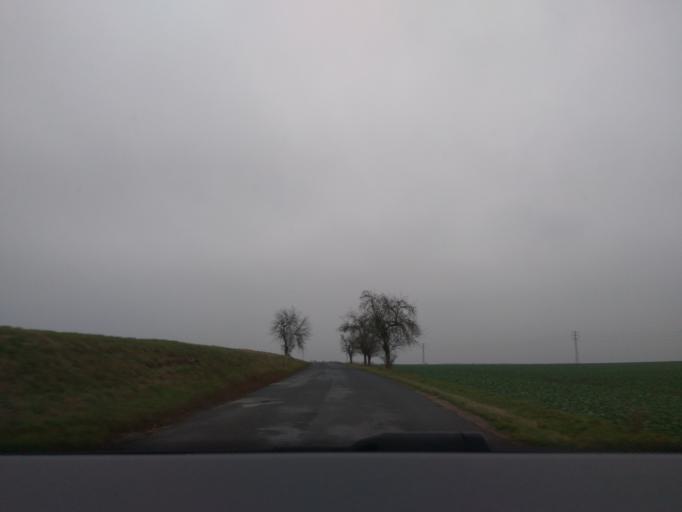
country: CZ
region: Praha
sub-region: Praha 19
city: Kbely
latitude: 50.1679
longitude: 14.5606
